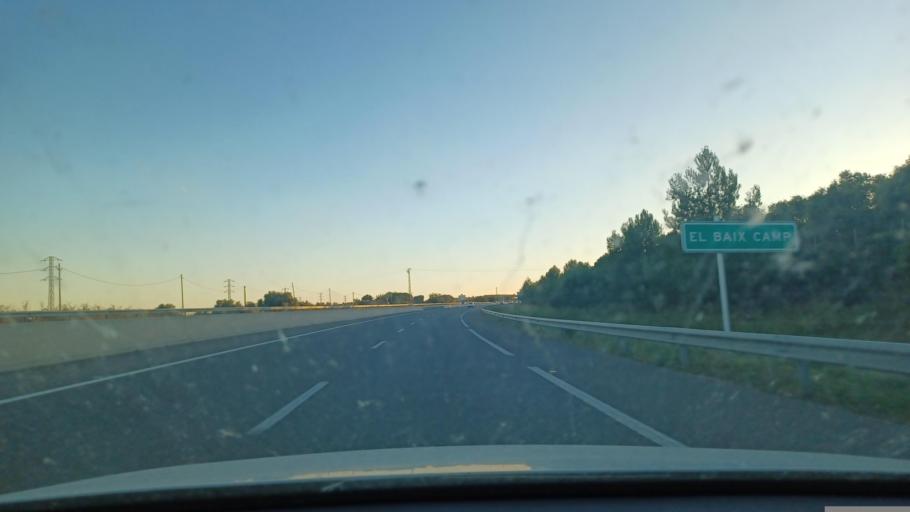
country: ES
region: Catalonia
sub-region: Provincia de Tarragona
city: La Selva
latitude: 41.2283
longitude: 1.1613
